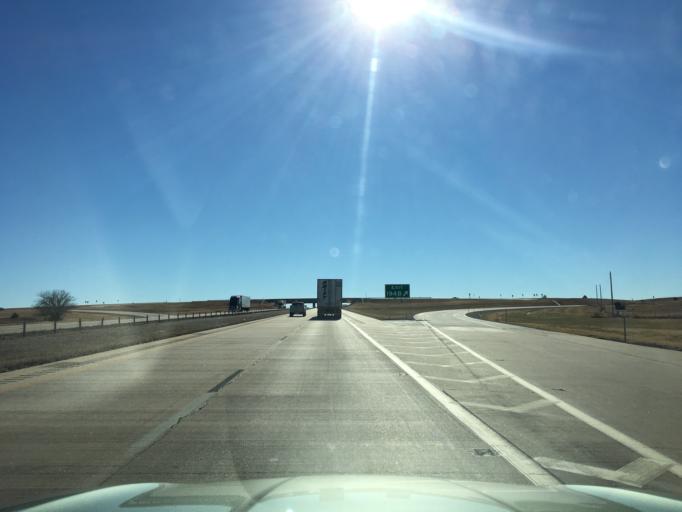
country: US
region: Oklahoma
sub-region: Noble County
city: Perry
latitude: 36.4047
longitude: -97.3272
